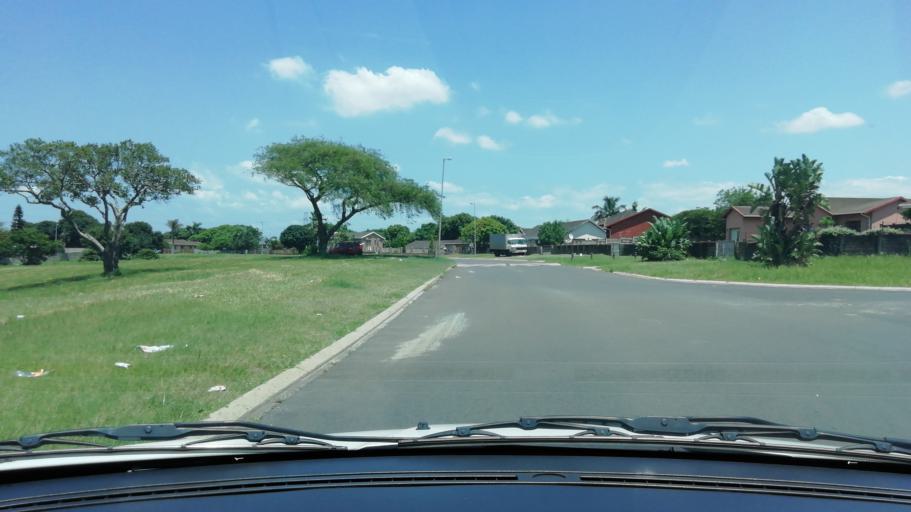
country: ZA
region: KwaZulu-Natal
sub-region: uThungulu District Municipality
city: Richards Bay
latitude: -28.7332
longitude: 32.0474
